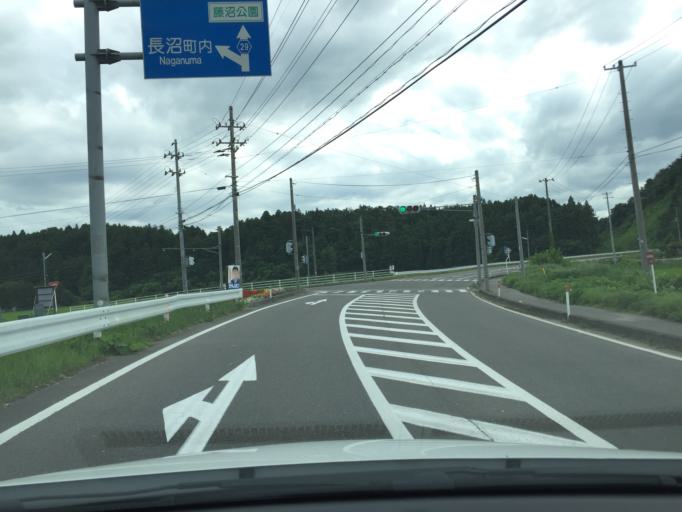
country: JP
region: Fukushima
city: Sukagawa
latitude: 37.2988
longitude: 140.2110
